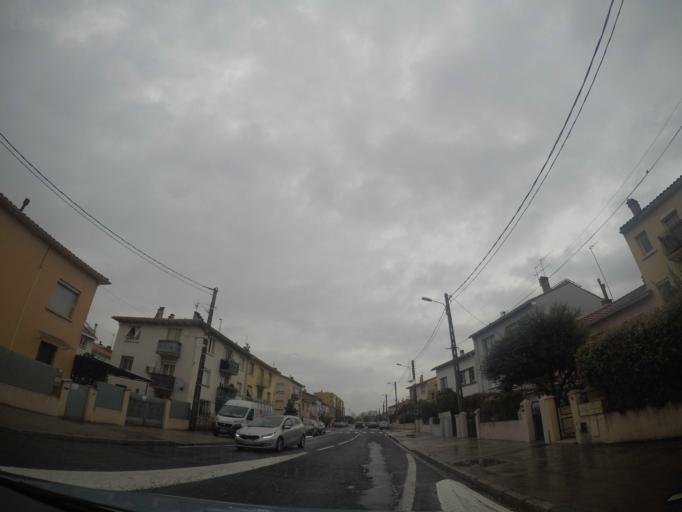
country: FR
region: Languedoc-Roussillon
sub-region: Departement des Pyrenees-Orientales
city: Perpignan
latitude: 42.6961
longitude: 2.8724
